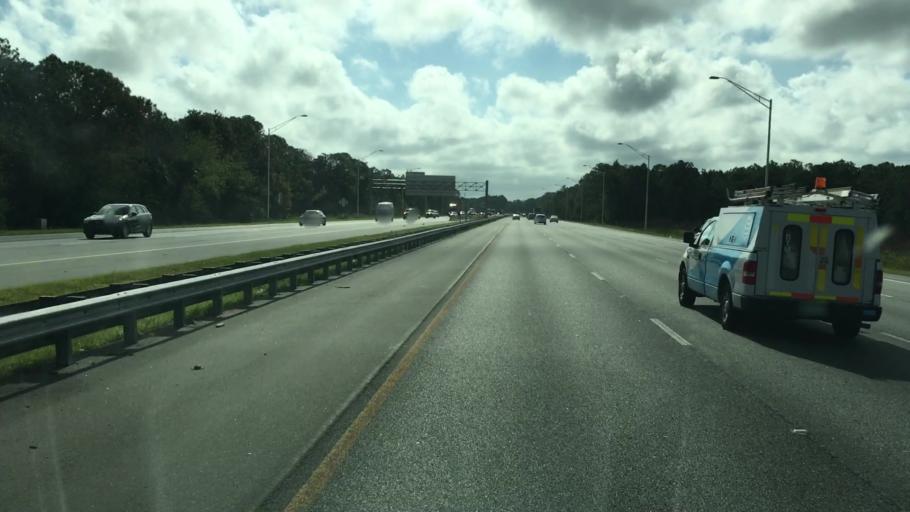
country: US
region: Florida
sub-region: Volusia County
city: South Daytona
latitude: 29.1414
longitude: -81.0678
